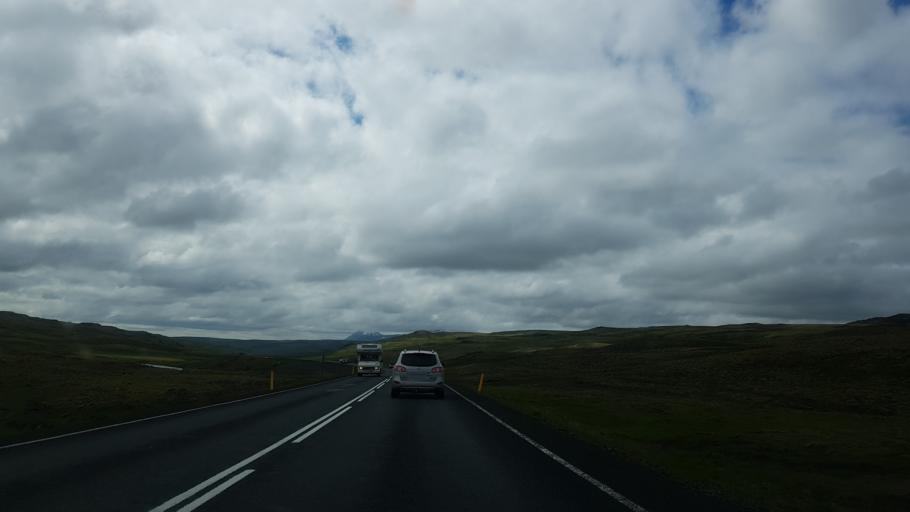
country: IS
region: West
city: Borgarnes
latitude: 64.9289
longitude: -21.0965
